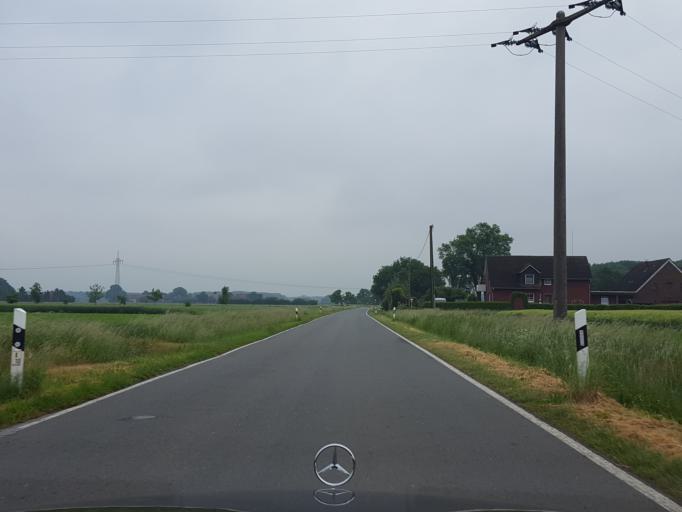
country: DE
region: North Rhine-Westphalia
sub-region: Regierungsbezirk Munster
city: Senden
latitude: 51.8291
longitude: 7.5613
